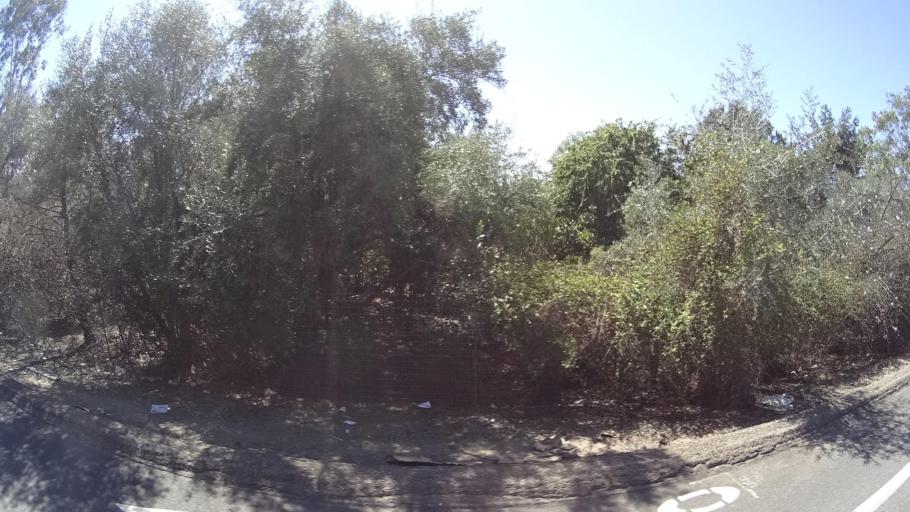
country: US
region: California
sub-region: San Diego County
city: Bonita
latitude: 32.6609
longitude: -117.0455
